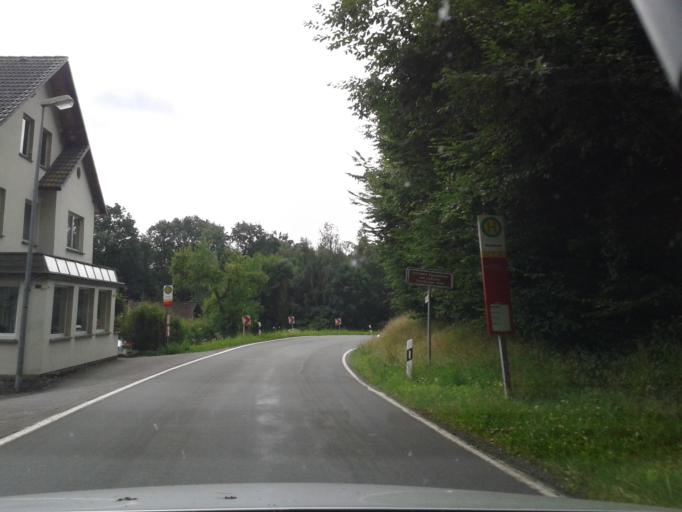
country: DE
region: North Rhine-Westphalia
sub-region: Regierungsbezirk Detmold
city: Barntrup
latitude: 51.9461
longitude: 9.1423
